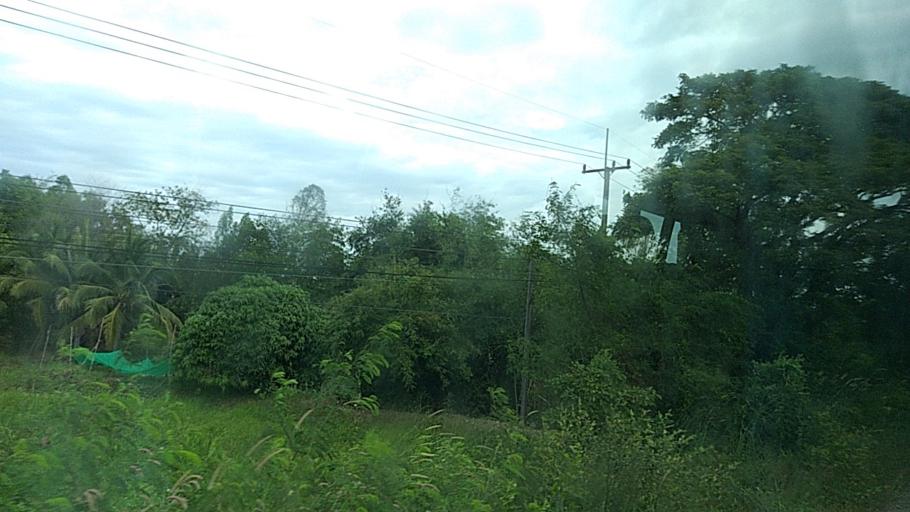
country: TH
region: Maha Sarakham
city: Kantharawichai
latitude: 16.3358
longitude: 103.2295
